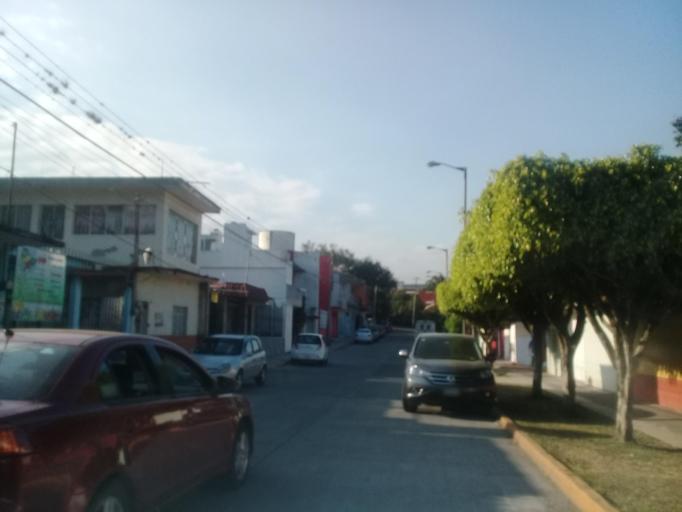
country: MX
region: Veracruz
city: Orizaba
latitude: 18.8543
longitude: -97.1134
